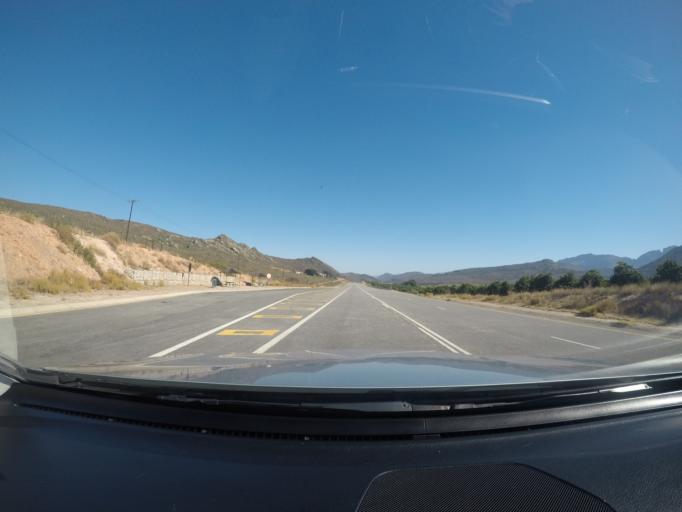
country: ZA
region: Western Cape
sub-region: West Coast District Municipality
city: Clanwilliam
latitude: -32.4575
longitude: 18.9600
